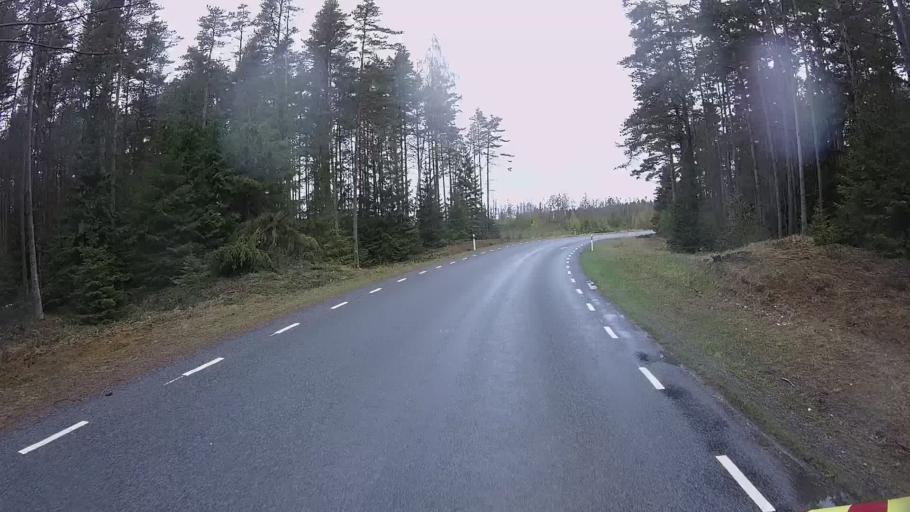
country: EE
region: Hiiumaa
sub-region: Kaerdla linn
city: Kardla
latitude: 58.9120
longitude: 22.3875
